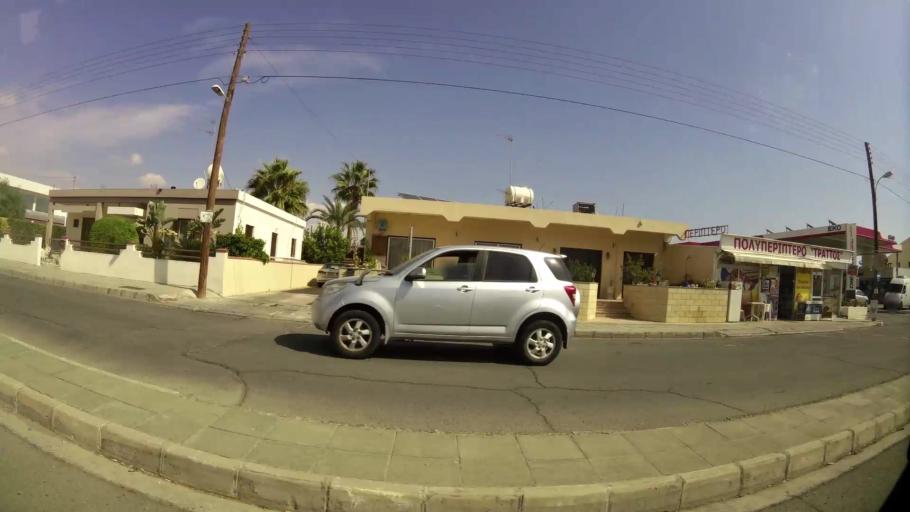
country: CY
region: Larnaka
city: Aradippou
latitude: 34.9355
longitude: 33.5924
